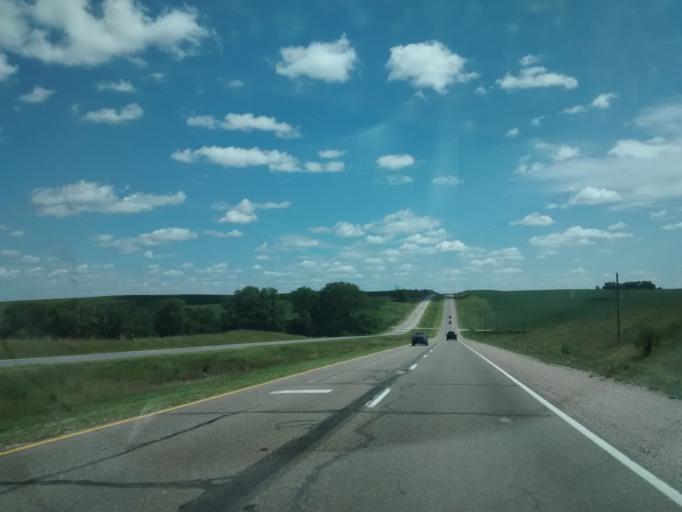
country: US
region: Iowa
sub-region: Woodbury County
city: Moville
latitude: 42.4749
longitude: -96.1593
